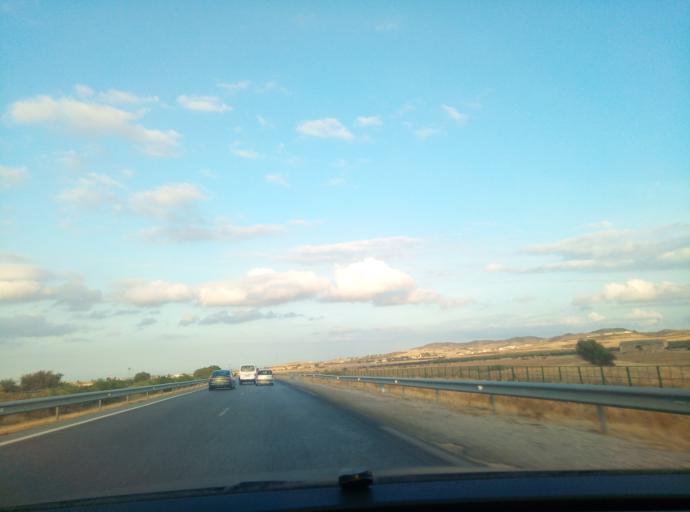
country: TN
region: Manouba
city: El Battan
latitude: 36.6661
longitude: 9.8760
